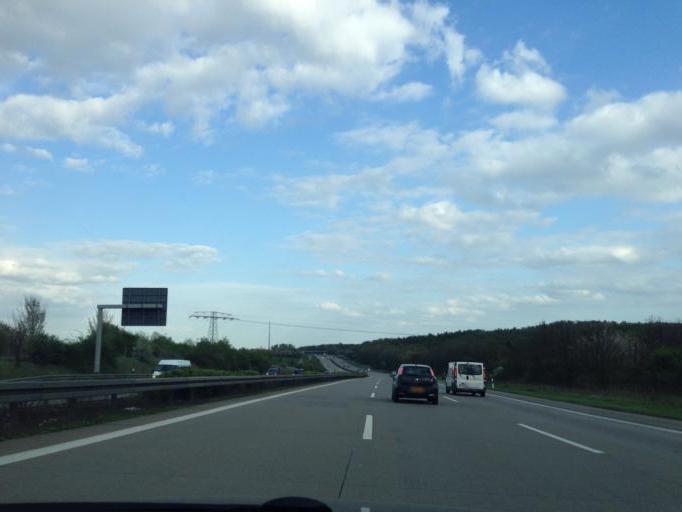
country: DE
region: Saxony-Anhalt
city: Beendorf
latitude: 52.2140
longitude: 11.0941
